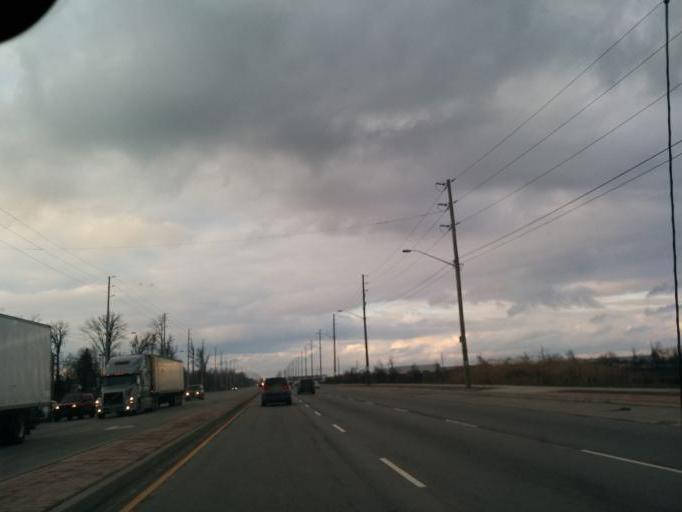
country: CA
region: Ontario
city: Brampton
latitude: 43.7852
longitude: -79.6587
